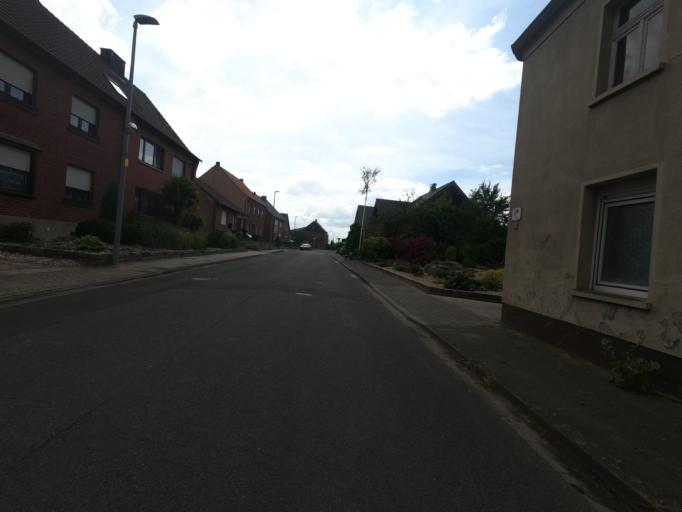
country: NL
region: Limburg
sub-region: Gemeente Roerdalen
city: Vlodrop
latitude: 51.1085
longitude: 6.1040
